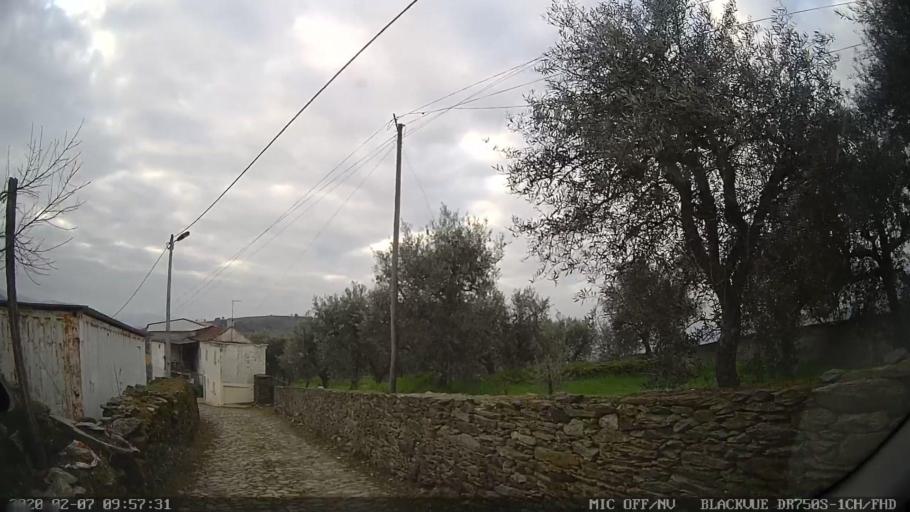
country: PT
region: Vila Real
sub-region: Sabrosa
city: Sabrosa
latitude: 41.2099
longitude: -7.5294
